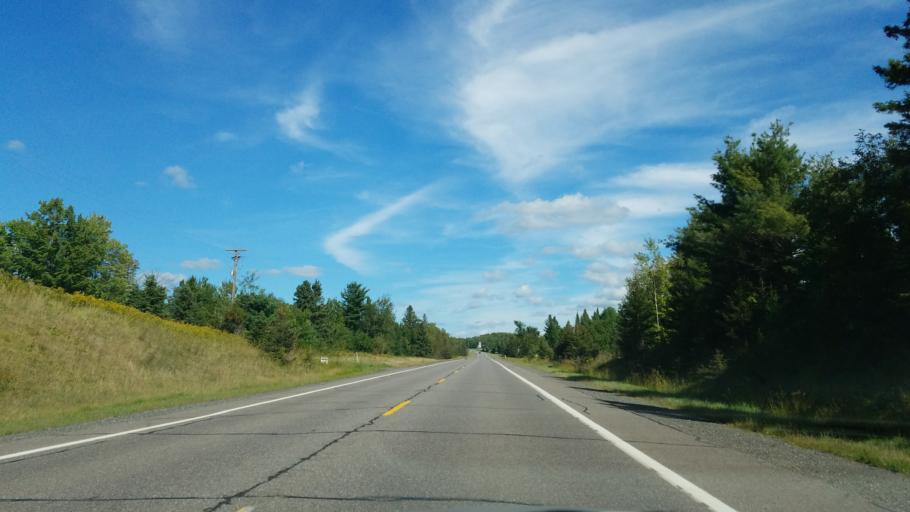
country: US
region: Michigan
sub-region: Baraga County
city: L'Anse
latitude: 46.5454
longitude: -88.5525
